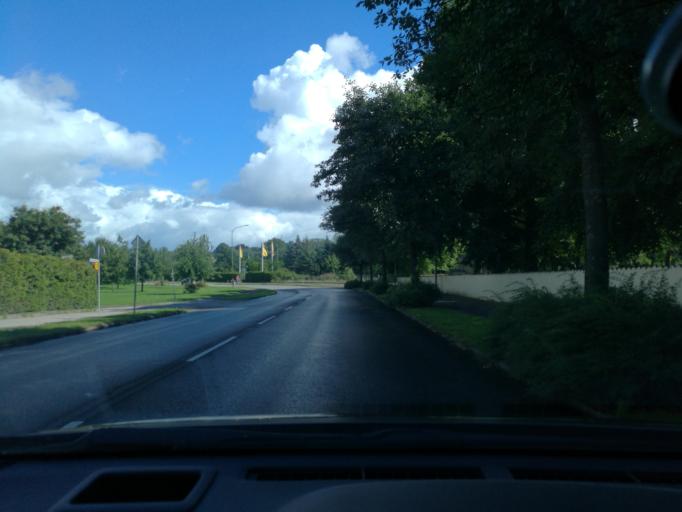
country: SE
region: Skane
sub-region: Eslovs Kommun
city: Eslov
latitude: 55.8299
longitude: 13.3008
